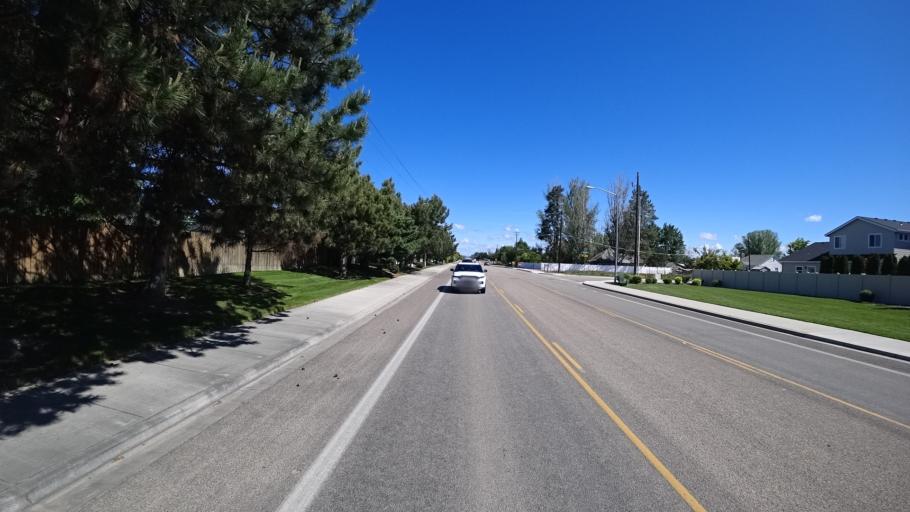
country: US
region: Idaho
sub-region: Ada County
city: Meridian
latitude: 43.6290
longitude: -116.3746
